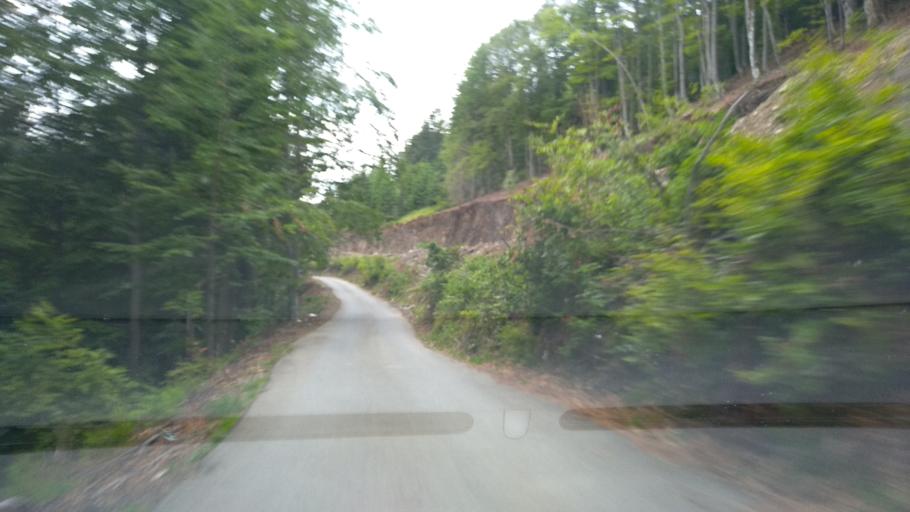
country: RO
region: Hunedoara
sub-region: Municipiul  Vulcan
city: Jiu-Paroseni
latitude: 45.3218
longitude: 23.2944
